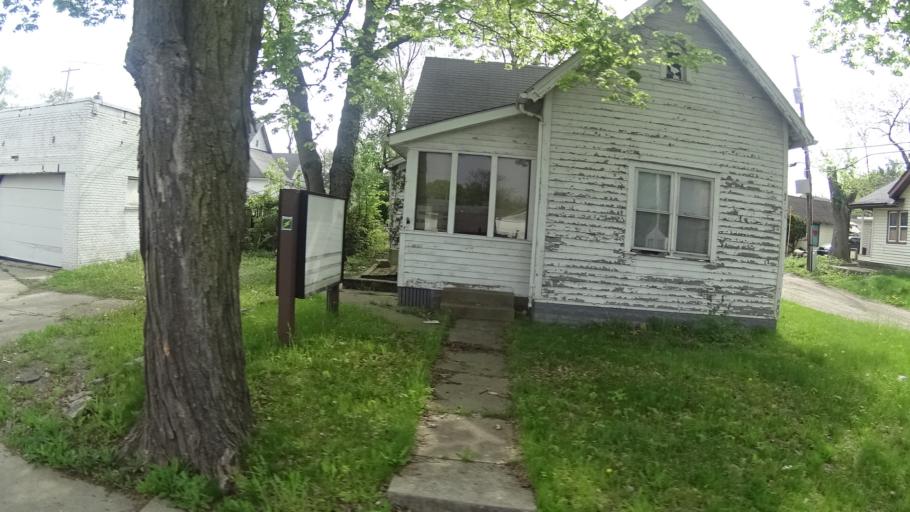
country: US
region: Indiana
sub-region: Madison County
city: Anderson
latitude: 40.1123
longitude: -85.6918
